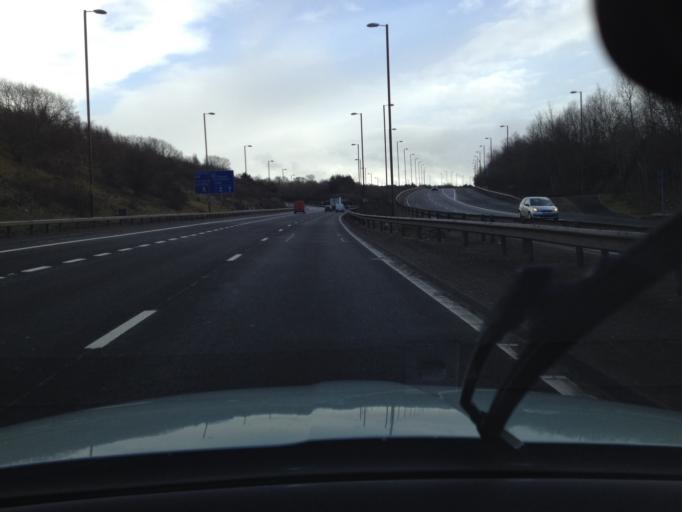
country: GB
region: Scotland
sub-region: Edinburgh
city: Newbridge
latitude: 55.9333
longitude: -3.4006
